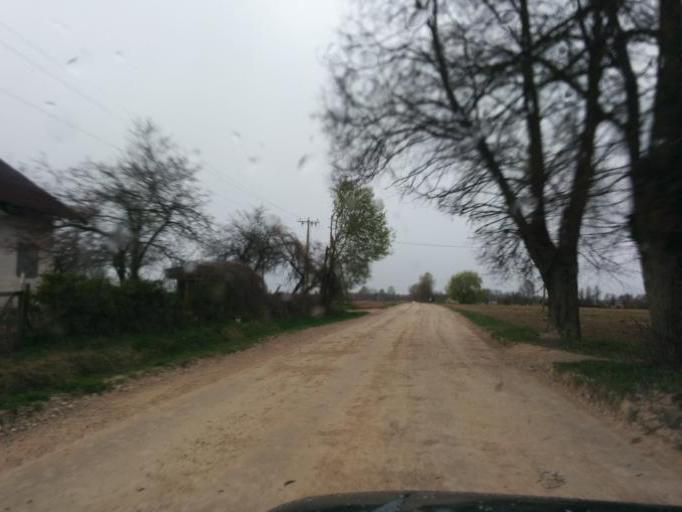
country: LV
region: Lecava
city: Iecava
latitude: 56.6003
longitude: 24.1865
